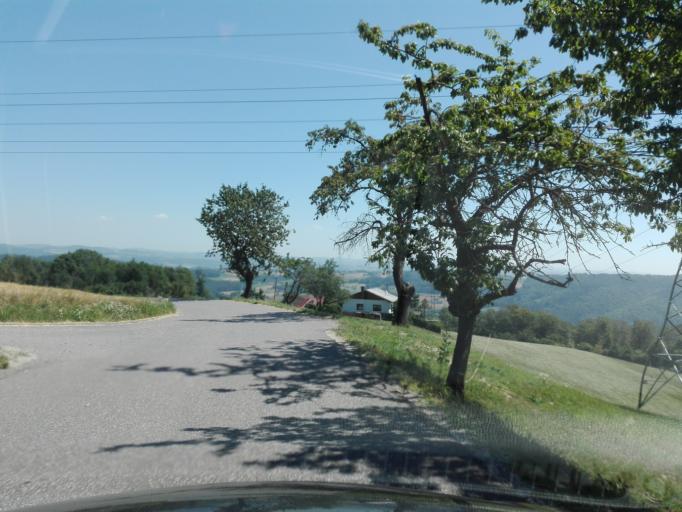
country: AT
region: Upper Austria
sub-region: Politischer Bezirk Urfahr-Umgebung
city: Steyregg
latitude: 48.3049
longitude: 14.3776
